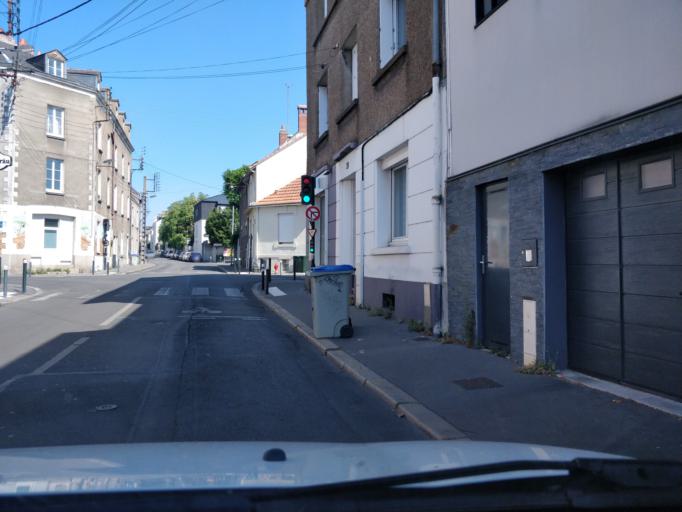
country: FR
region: Pays de la Loire
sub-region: Departement de la Loire-Atlantique
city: Nantes
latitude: 47.2235
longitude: -1.5379
